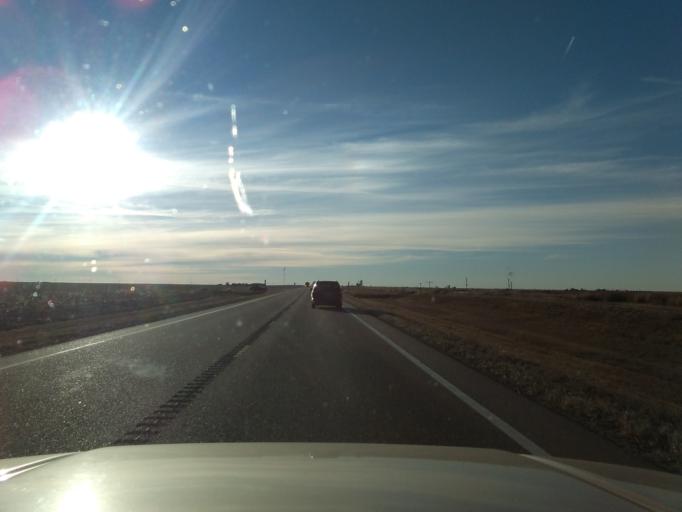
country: US
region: Kansas
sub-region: Thomas County
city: Colby
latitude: 39.4607
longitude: -100.7752
